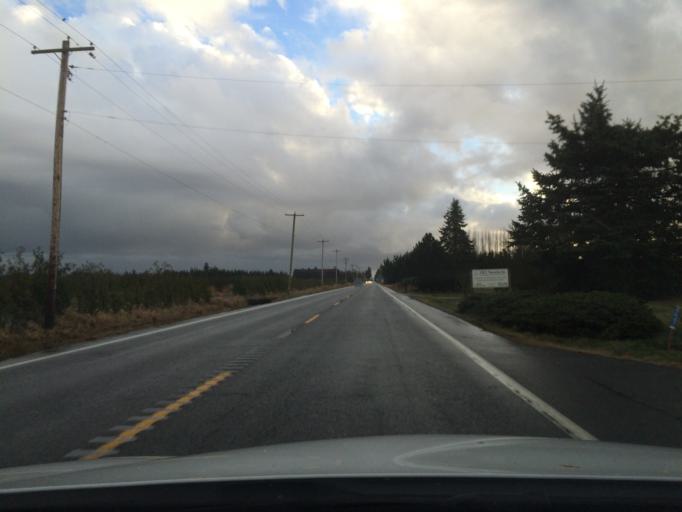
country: US
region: Washington
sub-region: Whatcom County
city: Lynden
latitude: 48.9552
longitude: -122.4852
